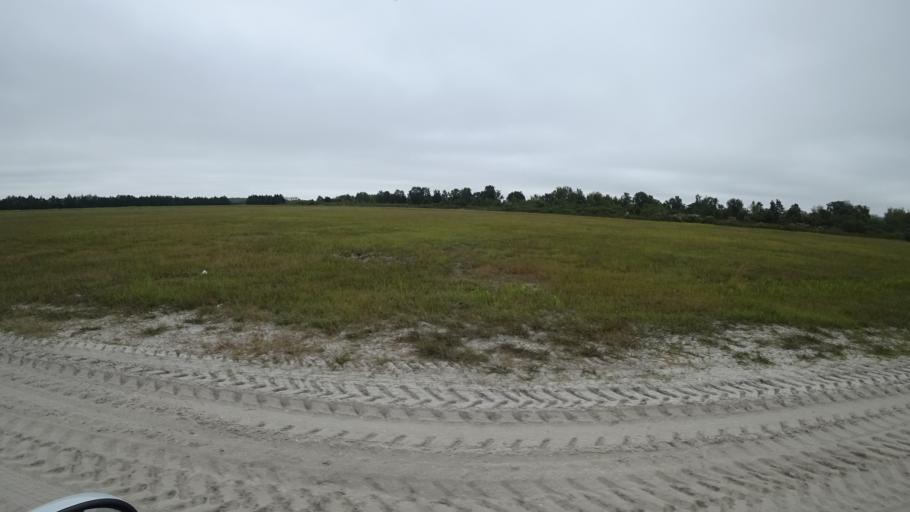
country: US
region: Florida
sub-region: Sarasota County
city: Warm Mineral Springs
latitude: 27.3001
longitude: -82.1256
